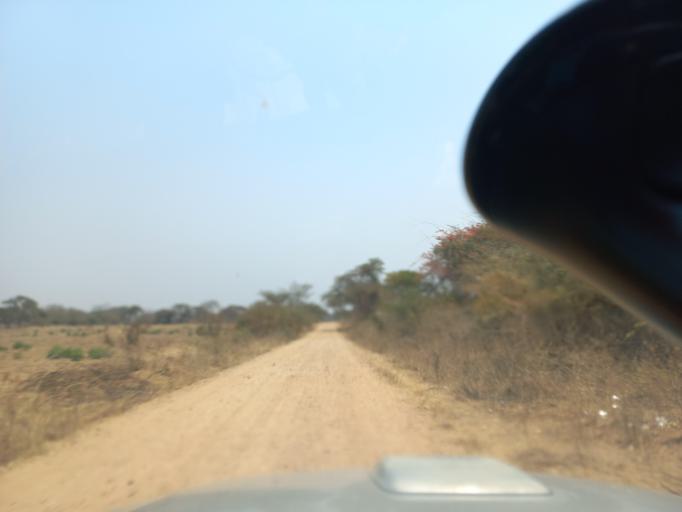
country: ZW
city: Chirundu
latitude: -15.9416
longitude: 28.8336
